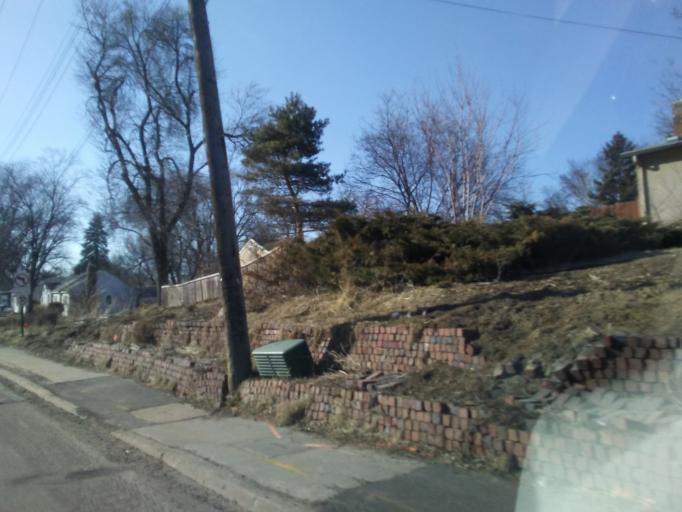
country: US
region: Minnesota
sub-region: Hennepin County
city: Richfield
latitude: 44.8835
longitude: -93.2977
